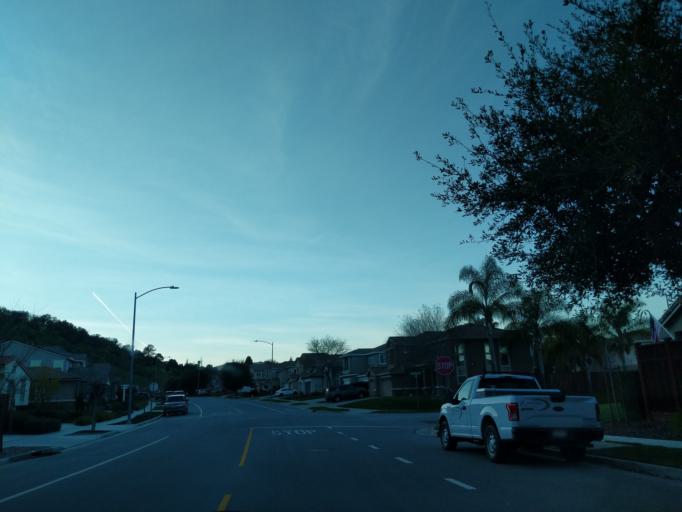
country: US
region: California
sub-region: Santa Clara County
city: Gilroy
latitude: 37.0317
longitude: -121.6120
